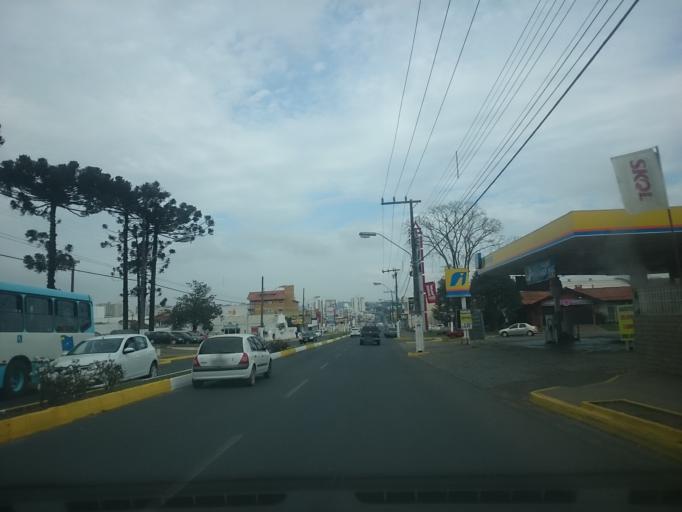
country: BR
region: Santa Catarina
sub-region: Lages
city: Lages
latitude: -27.8117
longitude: -50.3105
